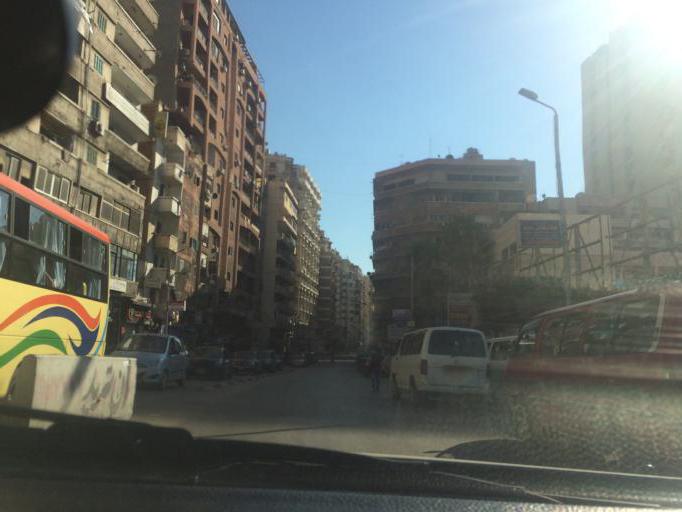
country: EG
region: Alexandria
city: Alexandria
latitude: 31.2477
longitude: 29.9784
